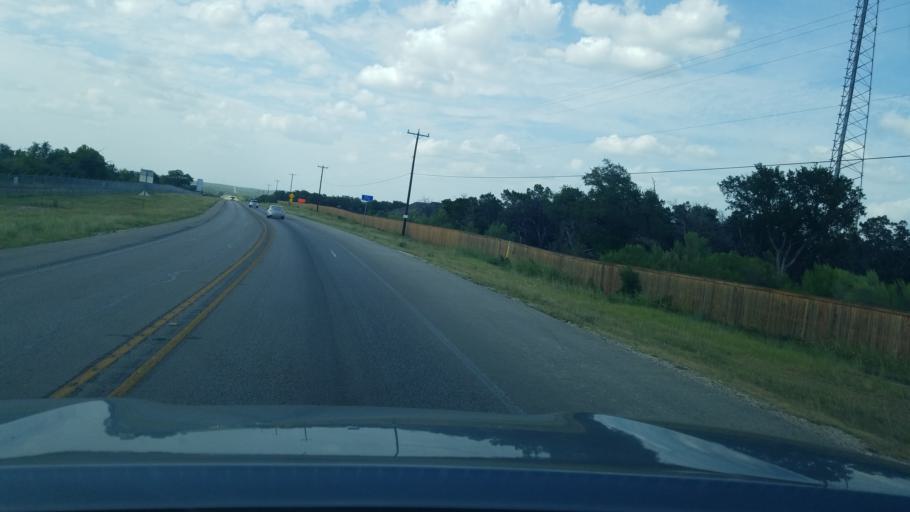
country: US
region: Texas
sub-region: Bexar County
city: Timberwood Park
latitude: 29.7143
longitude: -98.5130
